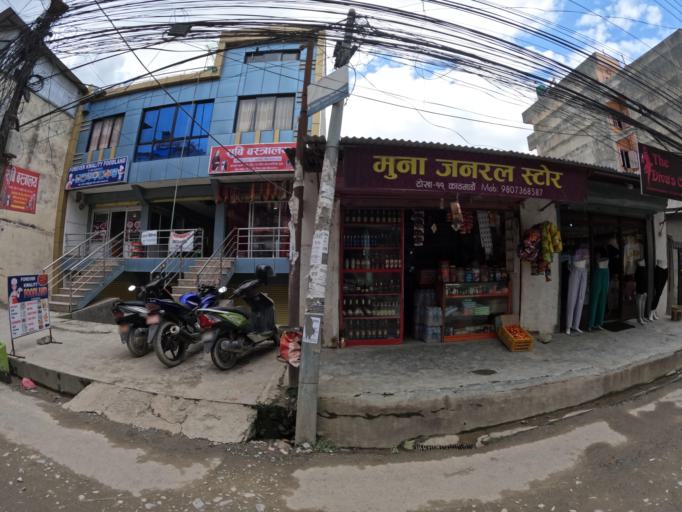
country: NP
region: Central Region
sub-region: Bagmati Zone
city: Kathmandu
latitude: 27.7425
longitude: 85.3152
